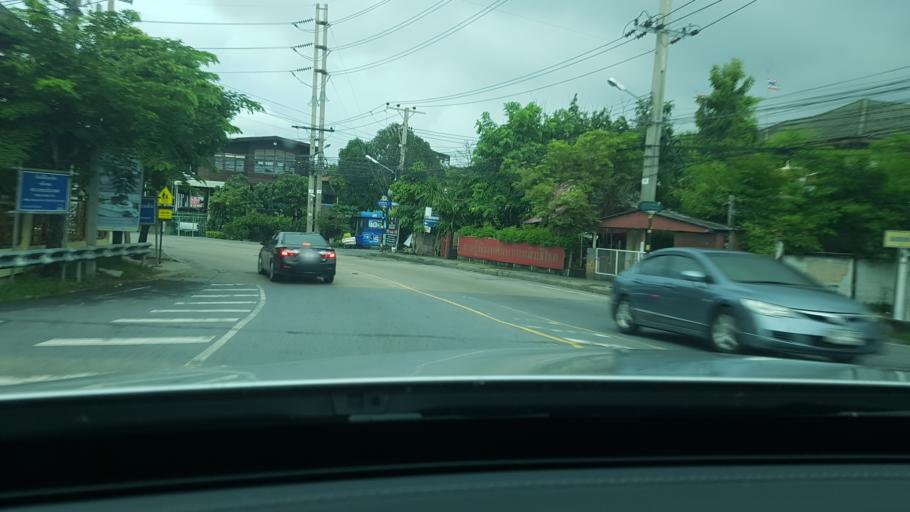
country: TH
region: Samut Prakan
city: Phra Pradaeng
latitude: 13.6679
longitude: 100.5195
